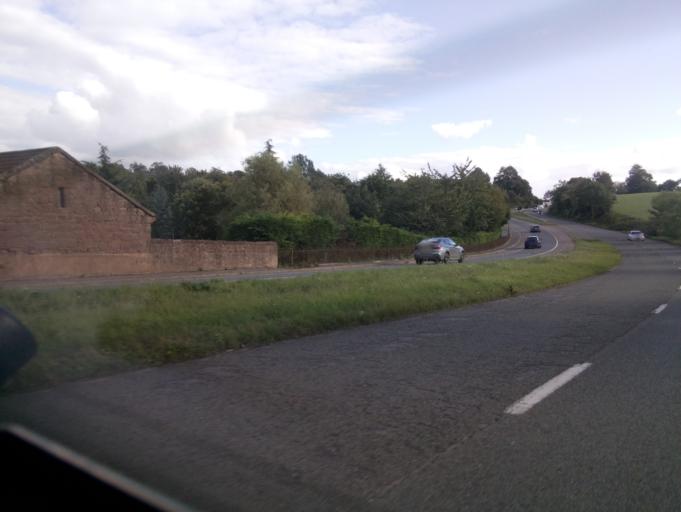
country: GB
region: England
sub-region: Devon
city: Exminster
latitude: 50.6829
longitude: -3.5324
